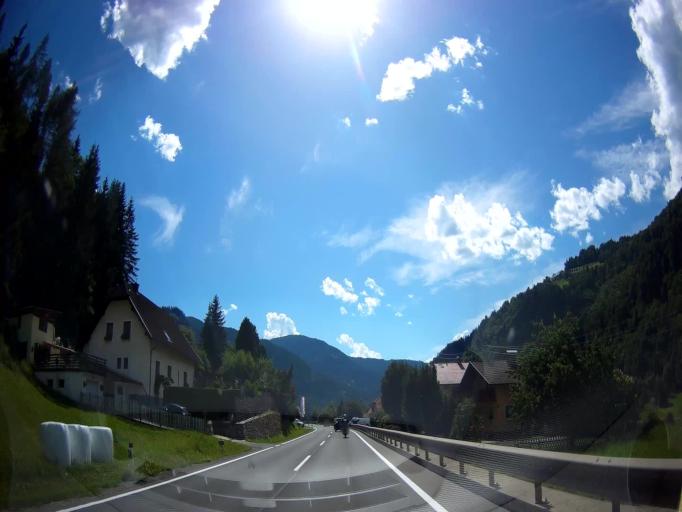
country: AT
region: Styria
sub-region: Politischer Bezirk Murau
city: Stadl an der Mur
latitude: 47.0734
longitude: 13.9177
